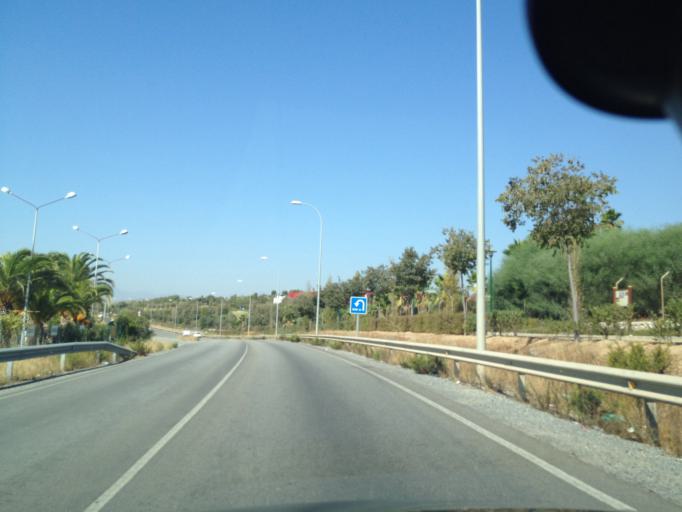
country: ES
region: Andalusia
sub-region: Provincia de Malaga
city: Estacion de Cartama
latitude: 36.7321
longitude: -4.5526
